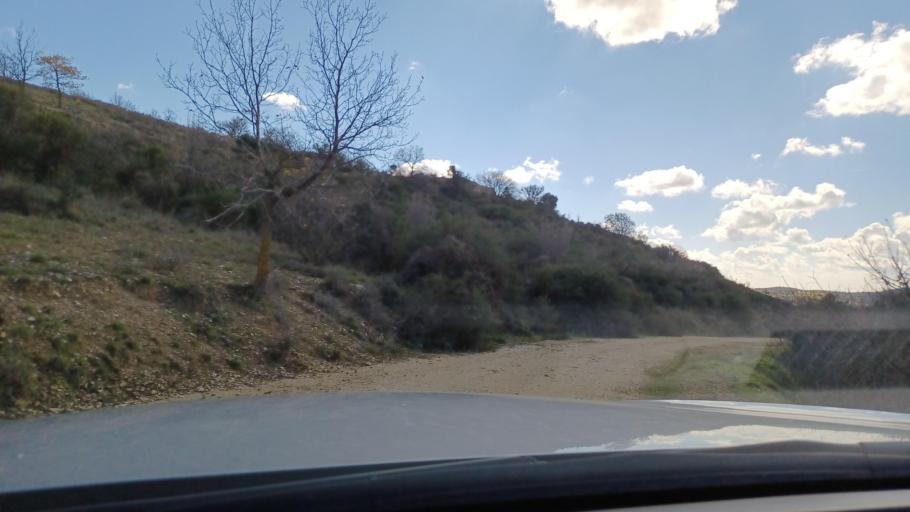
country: CY
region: Limassol
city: Pachna
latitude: 34.8221
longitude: 32.7681
